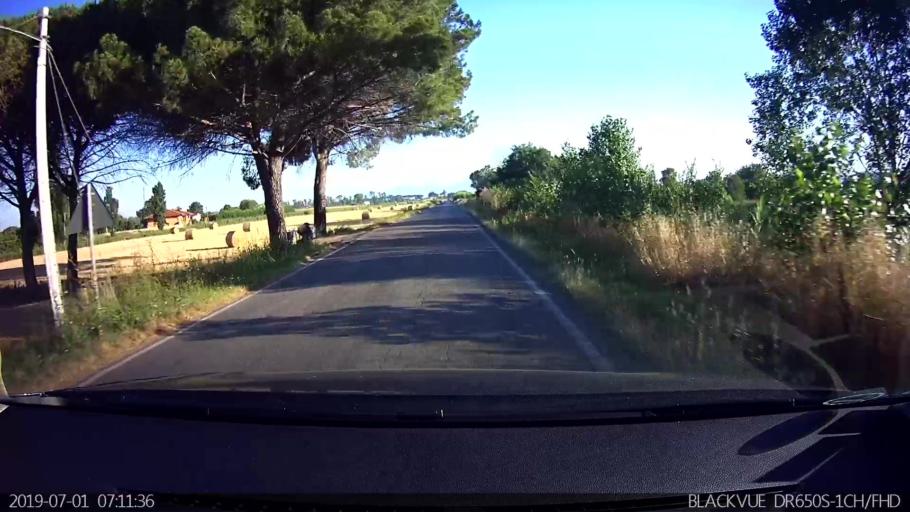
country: IT
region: Latium
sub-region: Provincia di Latina
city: Borgo Hermada
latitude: 41.3217
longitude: 13.1775
